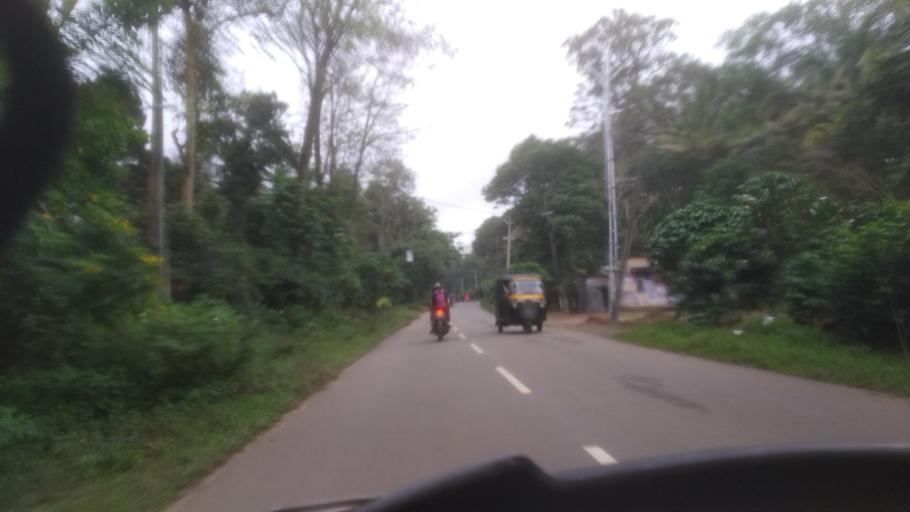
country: IN
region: Tamil Nadu
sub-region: Theni
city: Kombai
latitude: 9.8994
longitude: 77.1845
